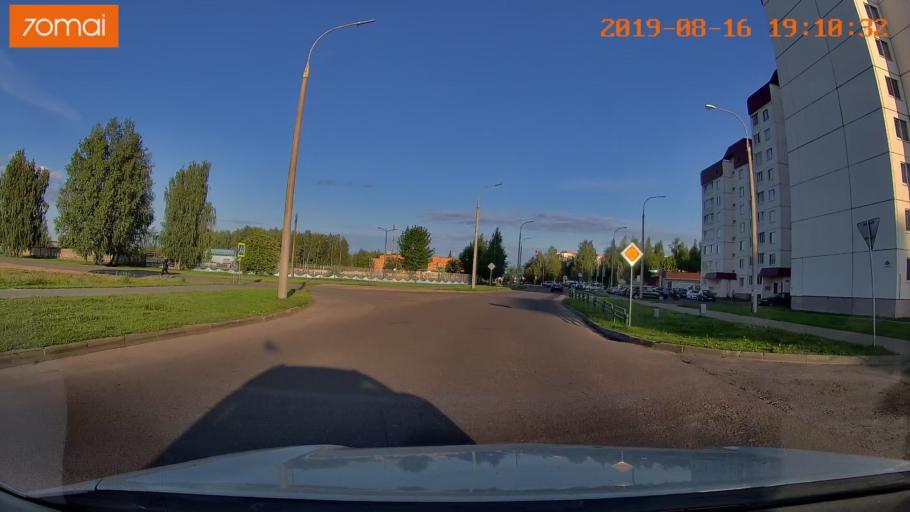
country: BY
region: Mogilev
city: Asipovichy
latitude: 53.3237
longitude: 28.6417
